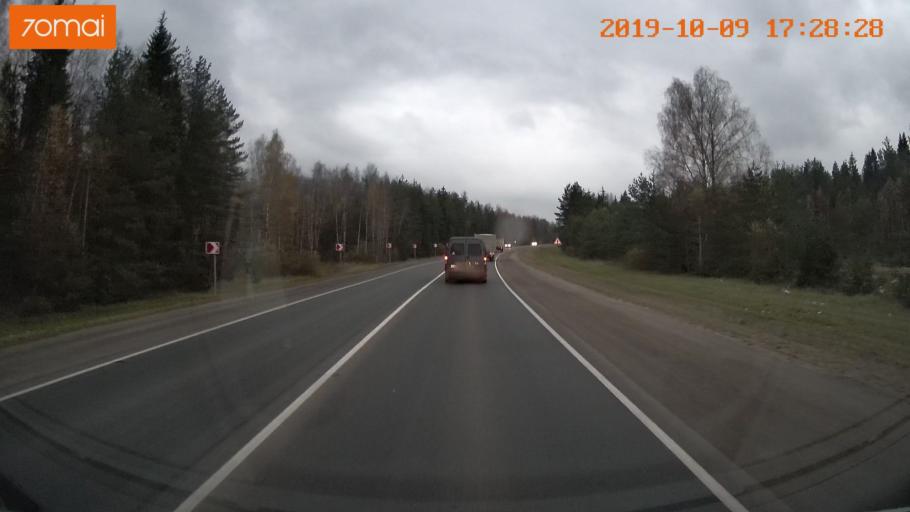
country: RU
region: Ivanovo
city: Furmanov
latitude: 57.1577
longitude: 41.0682
